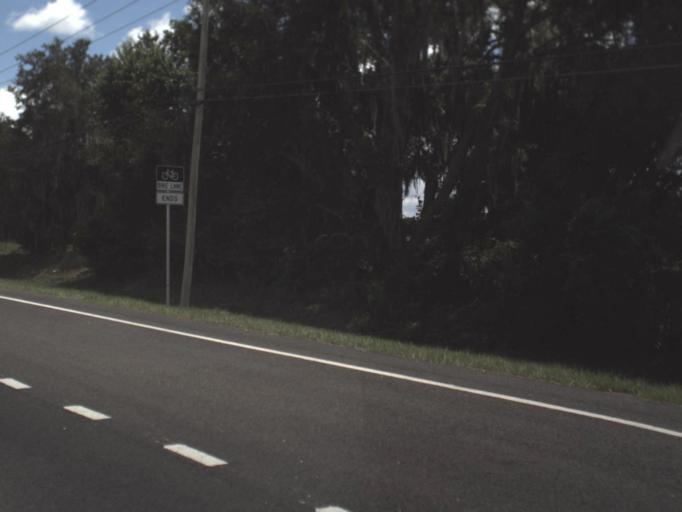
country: US
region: Florida
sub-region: Polk County
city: Wahneta
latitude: 27.9093
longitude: -81.7736
